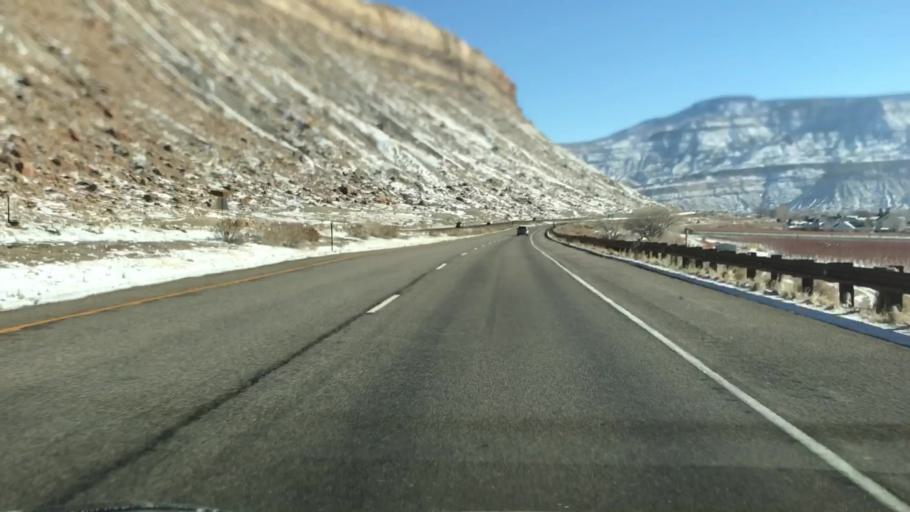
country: US
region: Colorado
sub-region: Mesa County
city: Palisade
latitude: 39.1203
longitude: -108.3719
